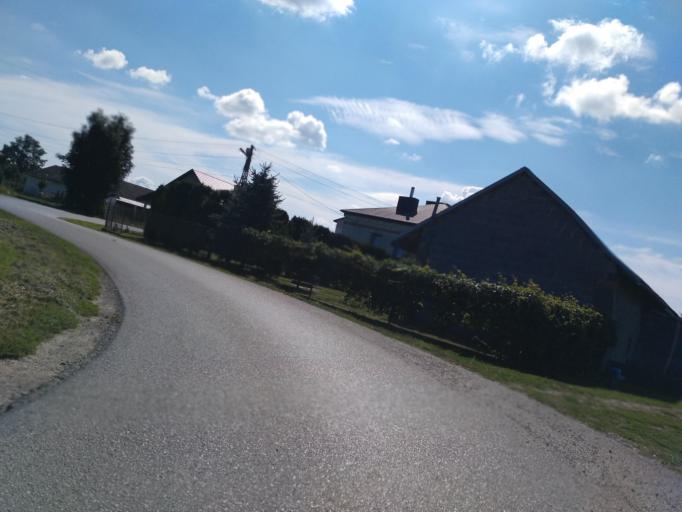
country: PL
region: Subcarpathian Voivodeship
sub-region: Powiat jasielski
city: Kolaczyce
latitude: 49.8068
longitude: 21.4159
